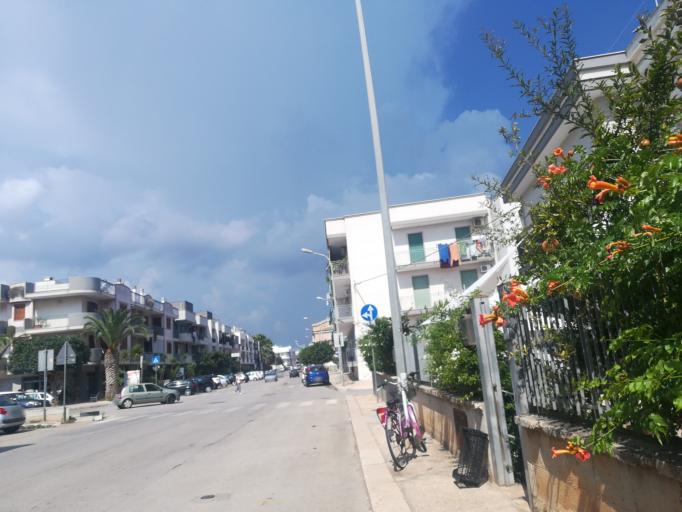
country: IT
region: Apulia
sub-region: Provincia di Bari
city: Polignano a Mare
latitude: 40.9894
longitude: 17.2241
